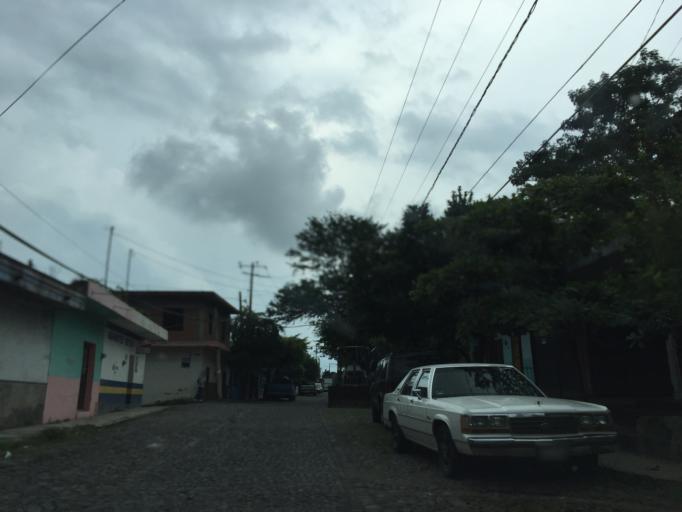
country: MX
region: Colima
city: Comala
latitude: 19.3288
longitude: -103.7598
